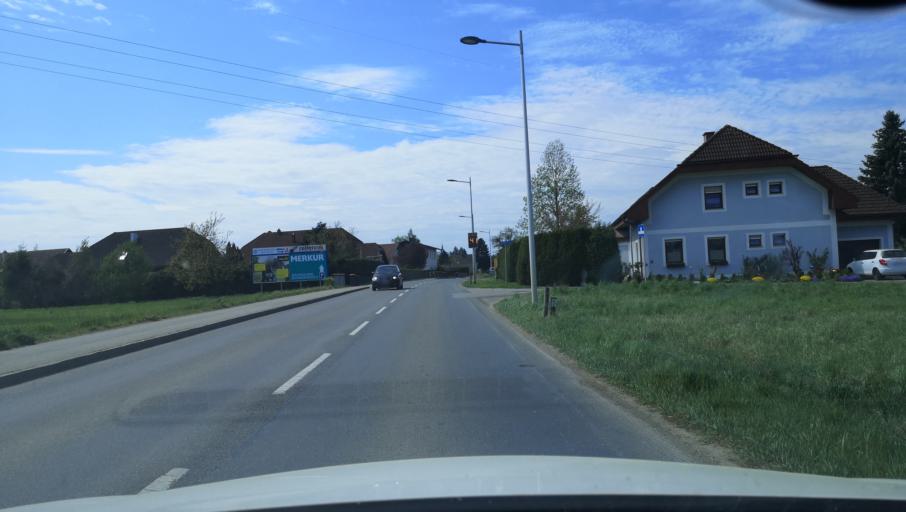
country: AT
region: Lower Austria
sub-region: Politischer Bezirk Melk
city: Petzenkirchen
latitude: 48.1381
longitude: 15.1453
